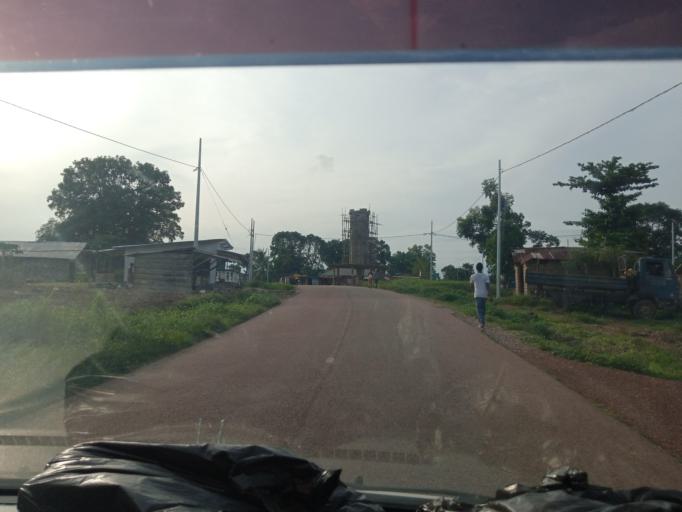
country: SL
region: Southern Province
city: Largo
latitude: 8.1998
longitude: -12.0594
